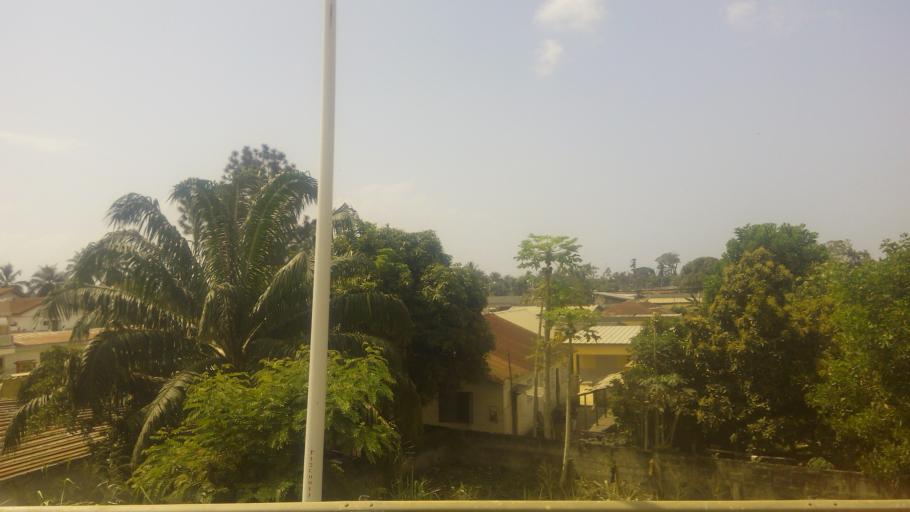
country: CI
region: Sud-Comoe
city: Grand-Bassam
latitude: 5.2212
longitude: -3.7235
